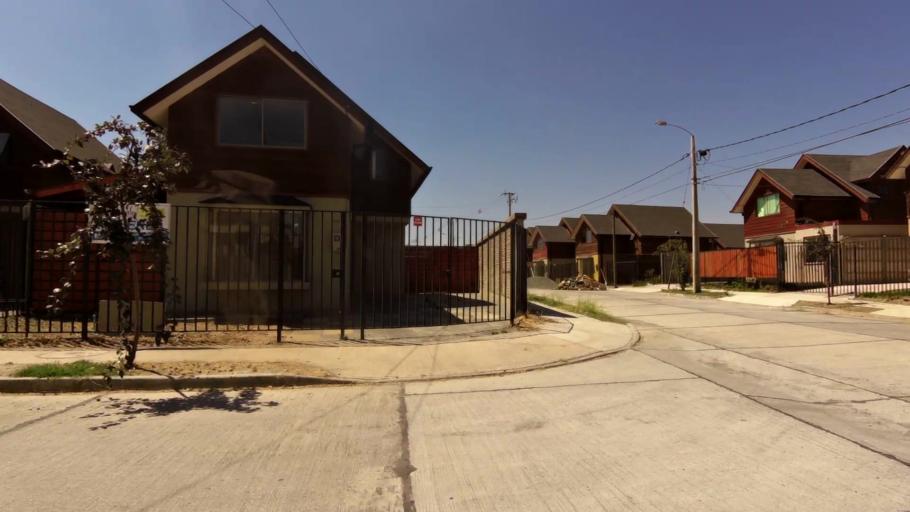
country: CL
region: Maule
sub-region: Provincia de Talca
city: Talca
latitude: -35.4269
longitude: -71.6168
